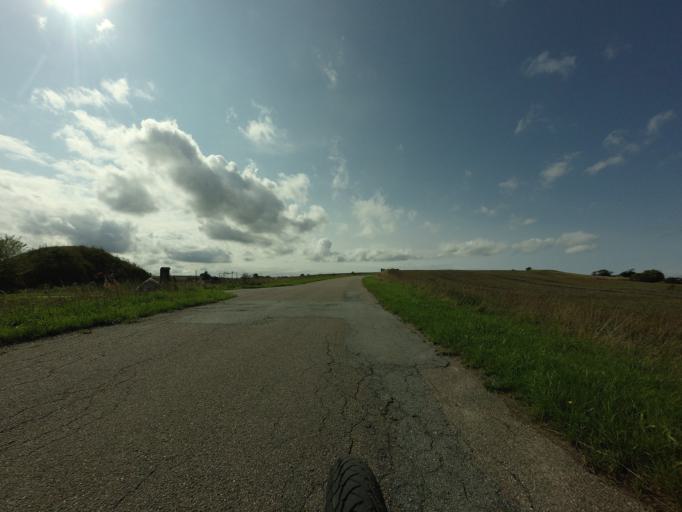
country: DK
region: North Denmark
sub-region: Hjorring Kommune
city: Hjorring
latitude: 57.5368
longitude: 10.0533
